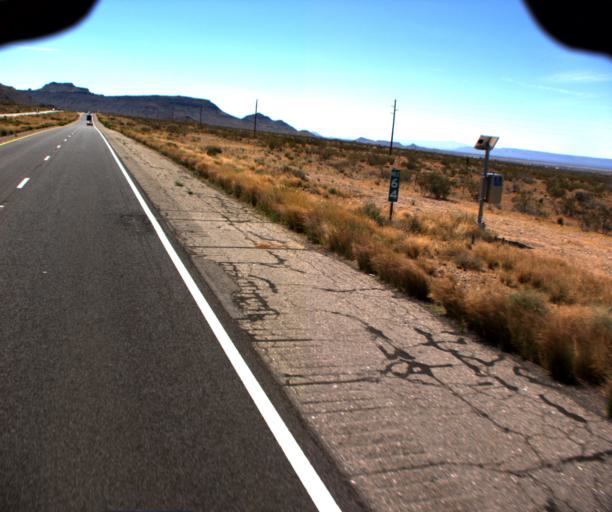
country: US
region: Arizona
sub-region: Mohave County
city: Golden Valley
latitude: 35.2565
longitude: -114.1579
